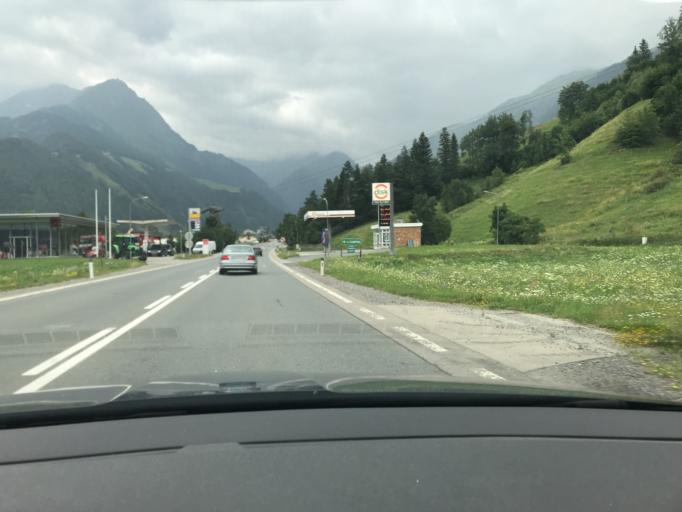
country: AT
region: Tyrol
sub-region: Politischer Bezirk Lienz
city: Matrei in Osttirol
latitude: 46.9891
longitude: 12.5453
